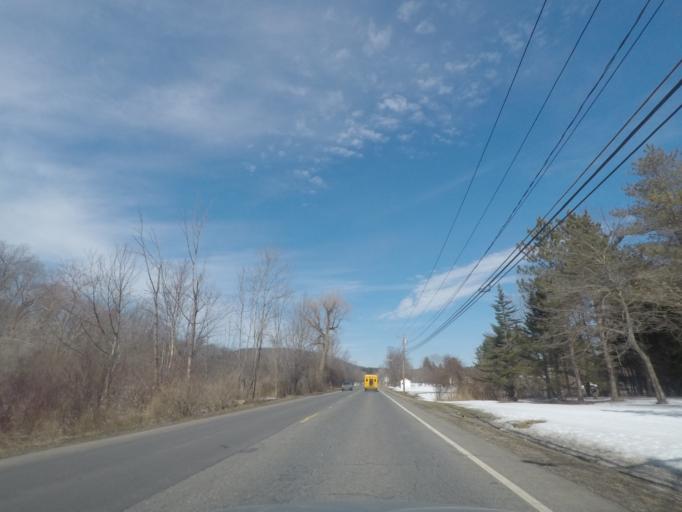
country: US
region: Massachusetts
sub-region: Berkshire County
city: Richmond
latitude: 42.4245
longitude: -73.3340
